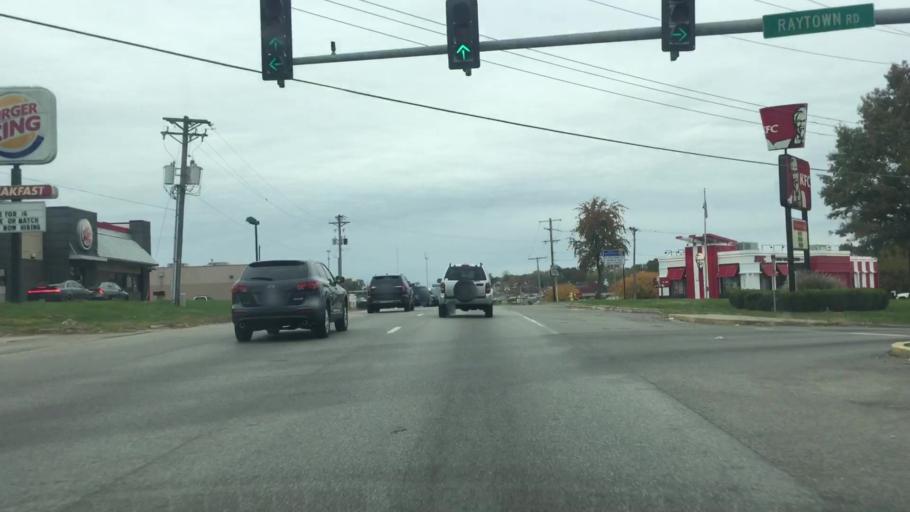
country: US
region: Missouri
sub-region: Jackson County
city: Raytown
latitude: 38.9881
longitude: -94.4643
